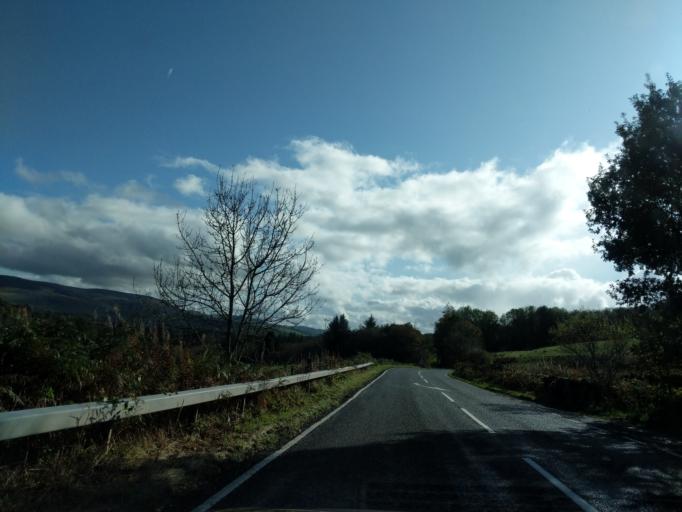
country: GB
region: Scotland
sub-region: Dumfries and Galloway
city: Moffat
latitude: 55.3436
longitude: -3.4598
